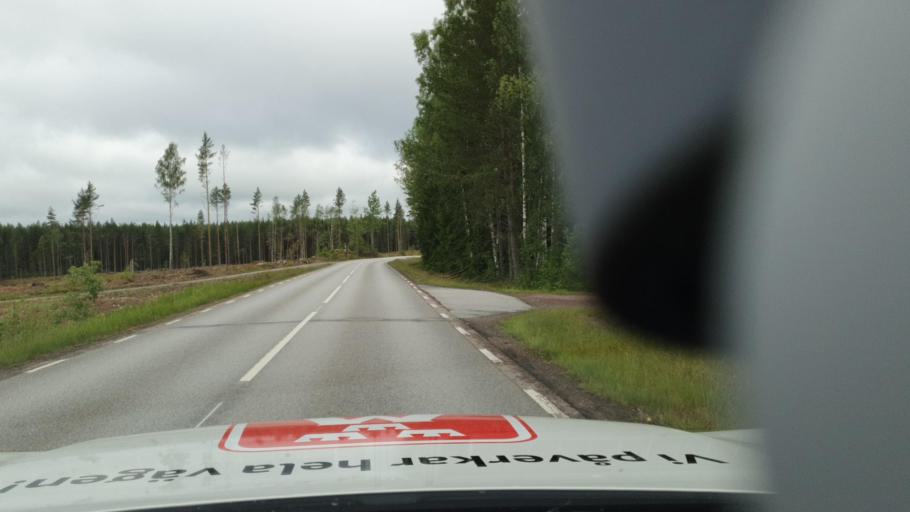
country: SE
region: Vaermland
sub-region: Kristinehamns Kommun
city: Bjorneborg
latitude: 59.1129
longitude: 14.2172
